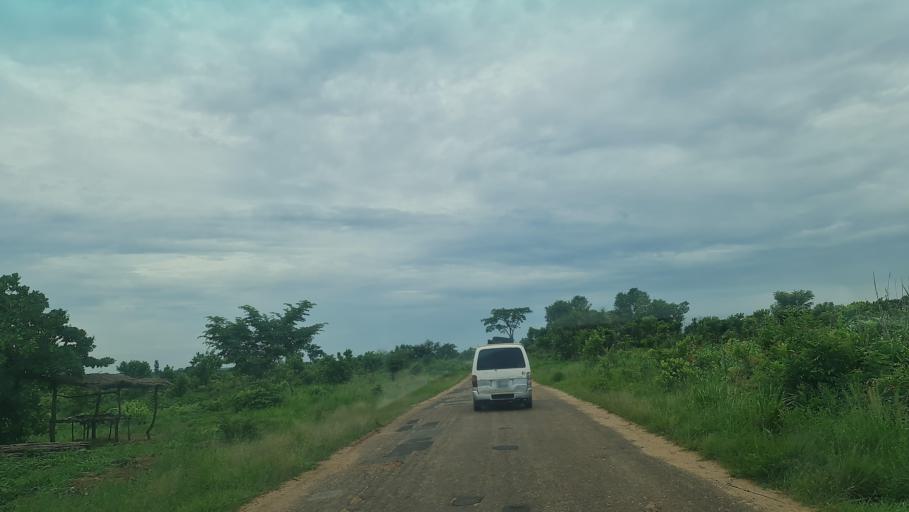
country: MW
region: Southern Region
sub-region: Nsanje District
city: Nsanje
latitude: -17.6829
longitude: 35.7261
